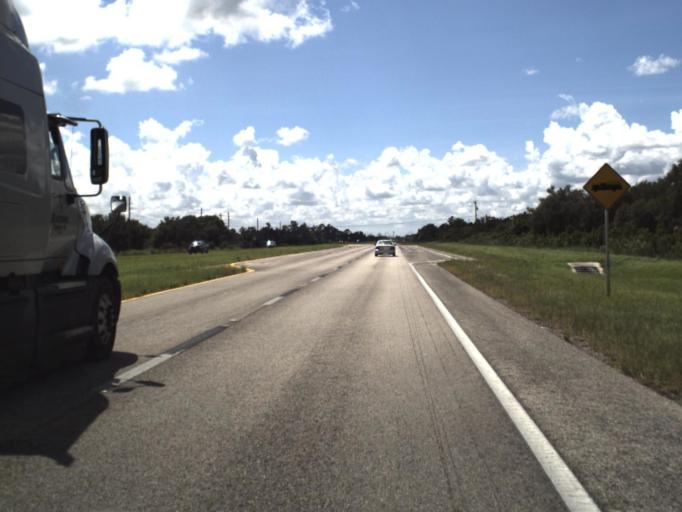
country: US
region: Florida
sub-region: Charlotte County
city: Harbour Heights
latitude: 27.0083
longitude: -81.9589
